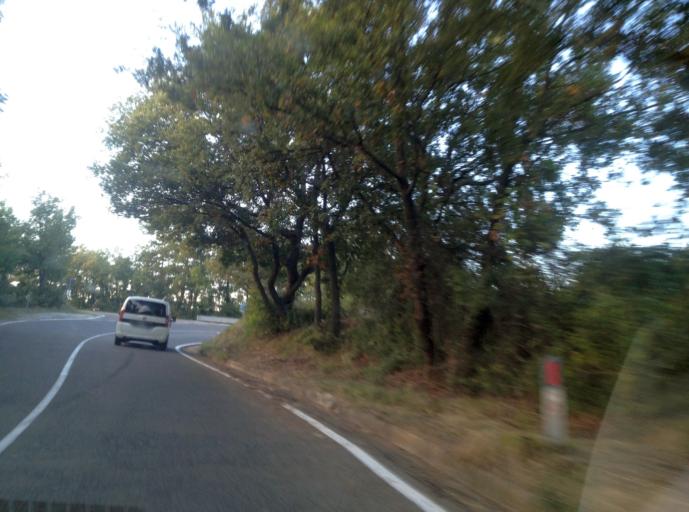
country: IT
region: Tuscany
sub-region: Provincia di Siena
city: Castellina in Chianti
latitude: 43.4262
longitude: 11.3058
